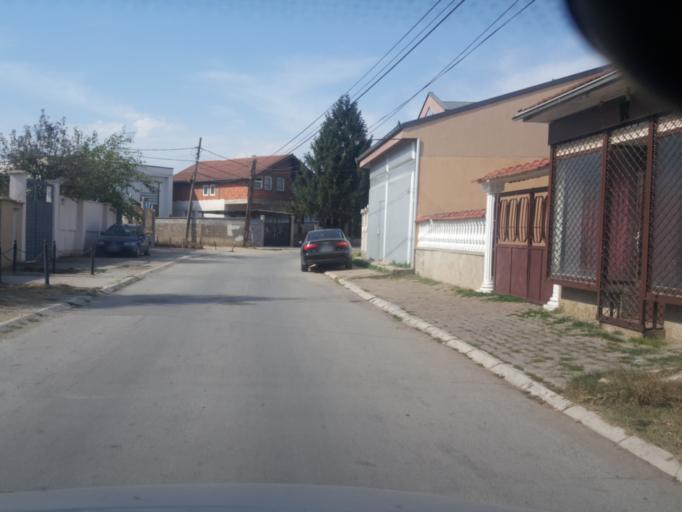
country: XK
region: Gjakova
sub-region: Komuna e Gjakoves
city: Gjakove
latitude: 42.3799
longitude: 20.4390
